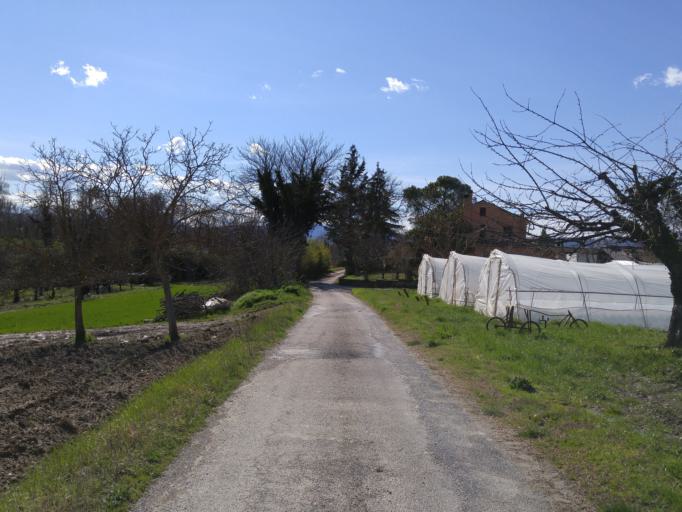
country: IT
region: The Marches
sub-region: Provincia di Pesaro e Urbino
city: Calcinelli
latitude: 43.7401
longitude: 12.9143
